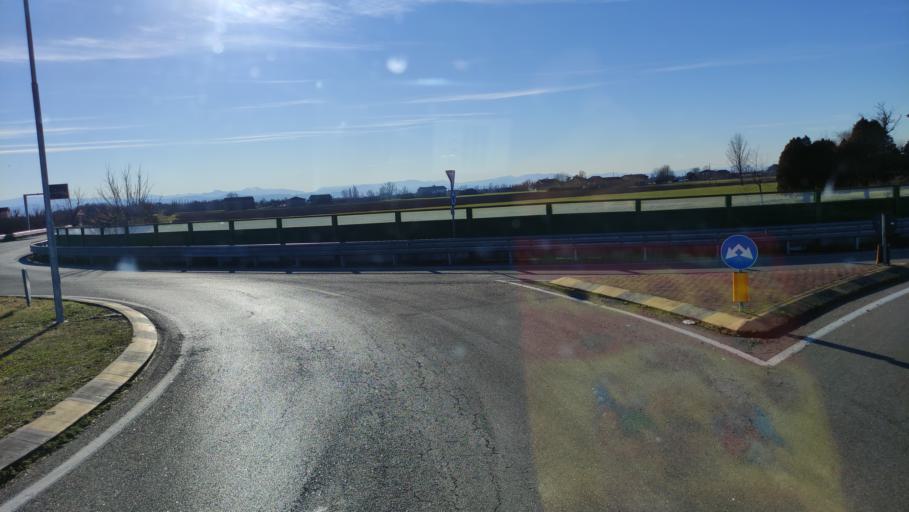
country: IT
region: Emilia-Romagna
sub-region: Provincia di Reggio Emilia
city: Bagnolo in Piano
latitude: 44.8007
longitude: 10.6826
